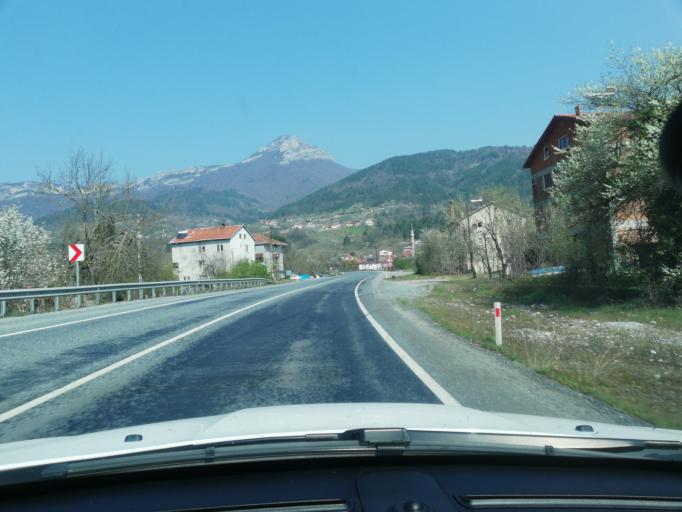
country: TR
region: Karabuk
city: Yenice
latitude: 41.2159
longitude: 32.2633
